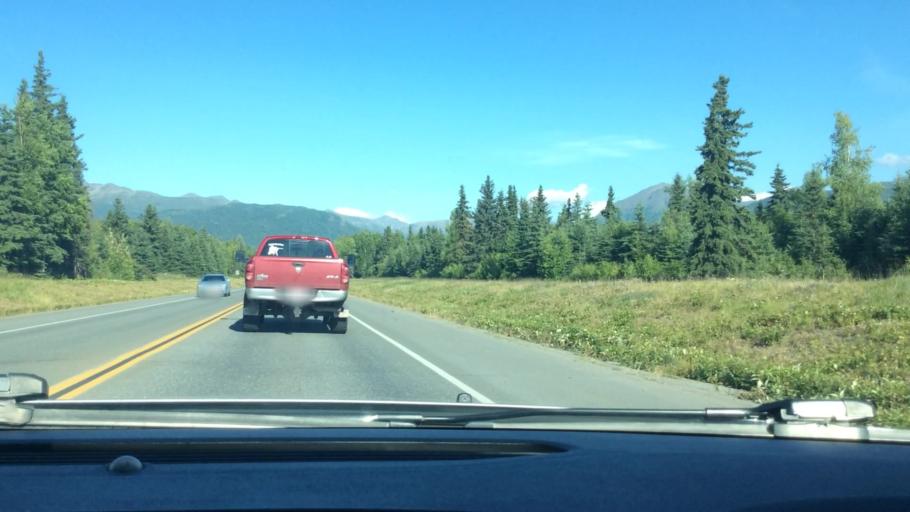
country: US
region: Alaska
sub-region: Anchorage Municipality
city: Elmendorf Air Force Base
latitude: 61.2399
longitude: -149.7203
